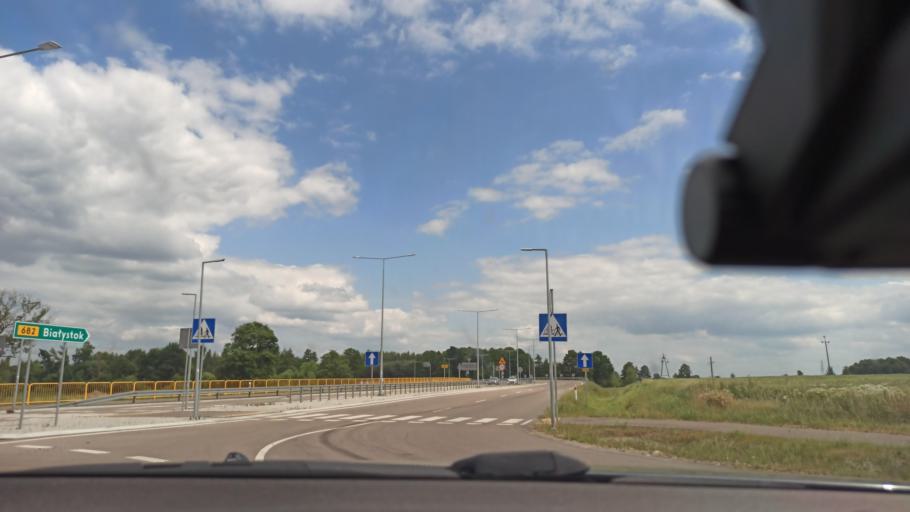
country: PL
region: Podlasie
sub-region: Powiat bialostocki
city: Turosn Koscielna
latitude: 53.0162
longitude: 23.0020
